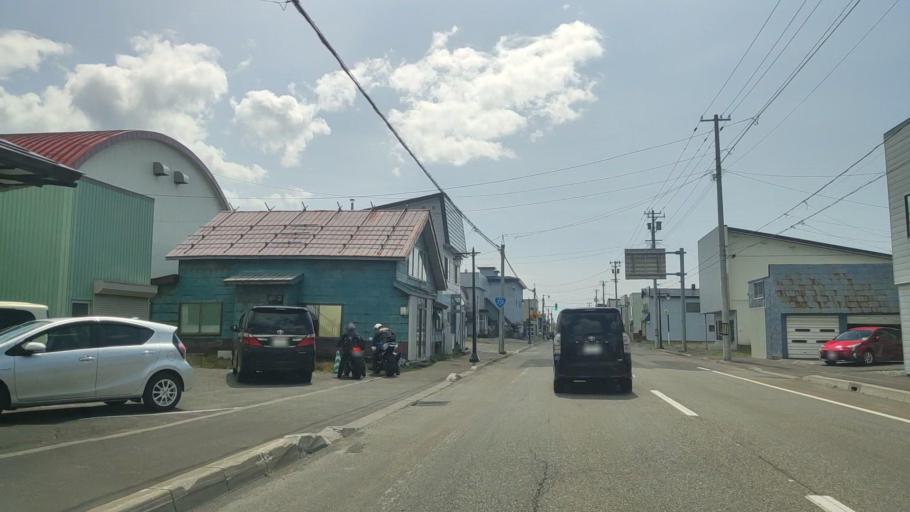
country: JP
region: Hokkaido
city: Makubetsu
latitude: 44.7255
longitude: 141.7989
